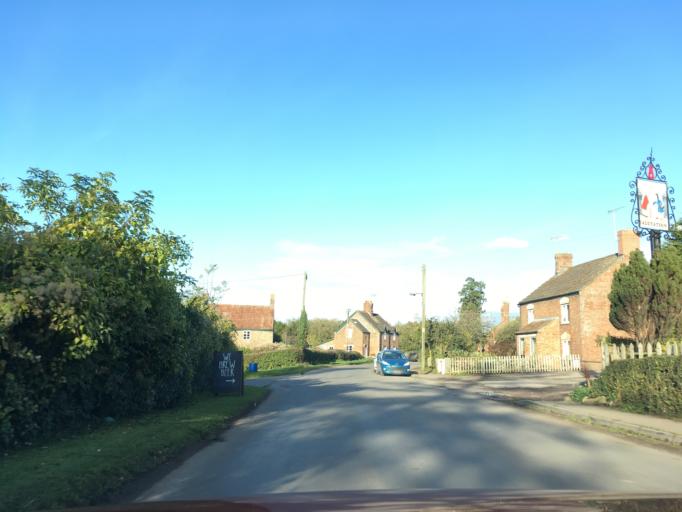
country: GB
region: England
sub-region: Gloucestershire
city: Berkeley
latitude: 51.6832
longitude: -2.4646
